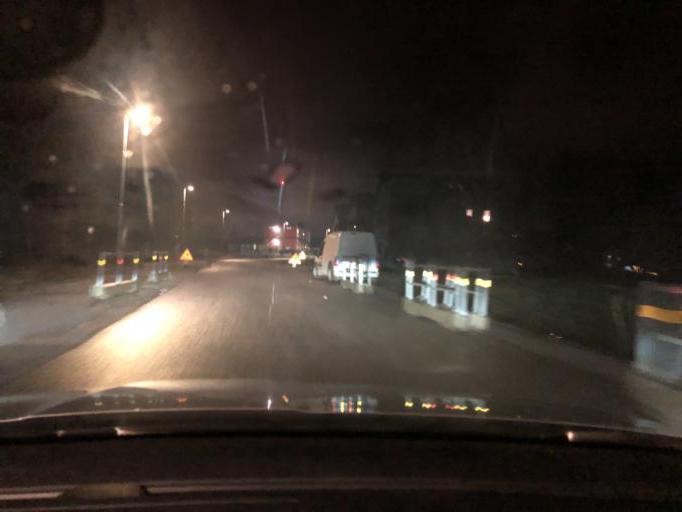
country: SE
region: Stockholm
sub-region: Botkyrka Kommun
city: Tumba
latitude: 59.2034
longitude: 17.8002
